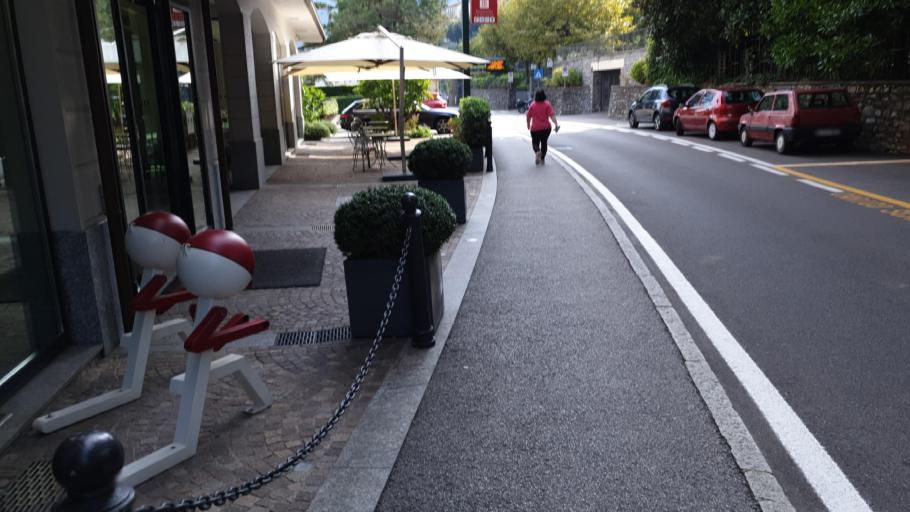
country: IT
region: Lombardy
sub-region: Provincia di Como
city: Bellagio
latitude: 45.9830
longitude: 9.2616
